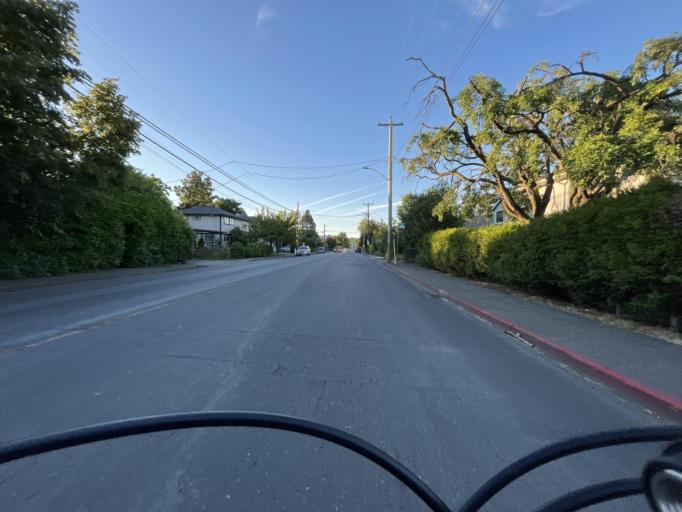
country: CA
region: British Columbia
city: Oak Bay
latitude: 48.4291
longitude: -123.3226
